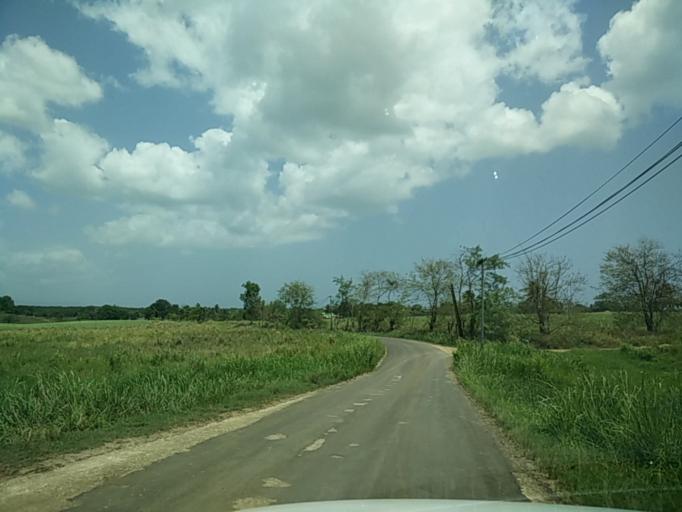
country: GP
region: Guadeloupe
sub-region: Guadeloupe
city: Les Abymes
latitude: 16.2817
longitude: -61.5183
